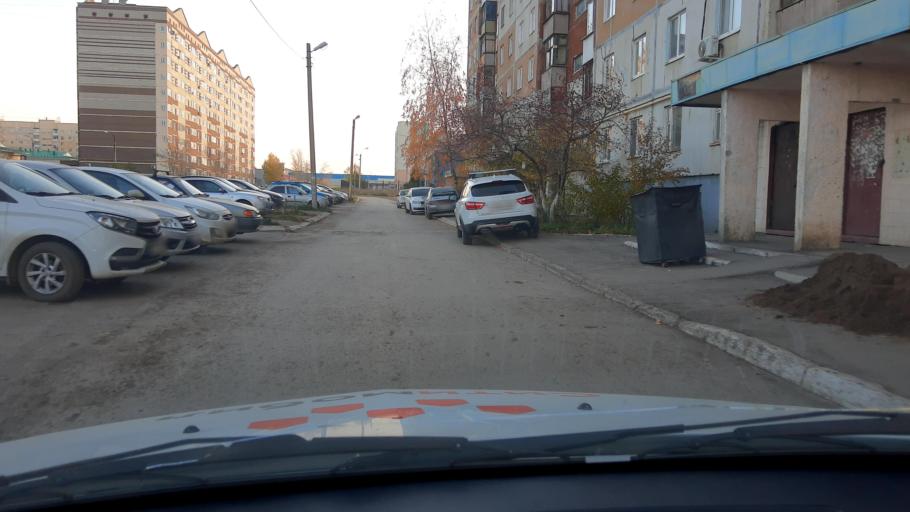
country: RU
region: Bashkortostan
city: Iglino
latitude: 54.7557
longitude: 56.2407
